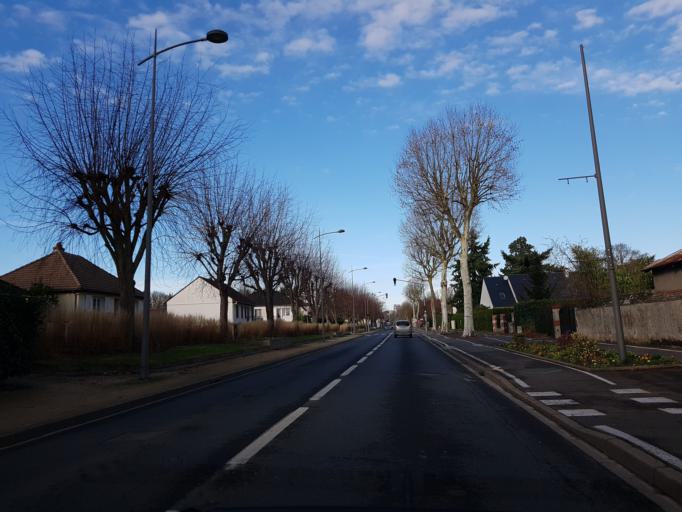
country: FR
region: Centre
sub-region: Departement du Loiret
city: Saint-Jean-le-Blanc
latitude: 47.8844
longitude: 1.9299
